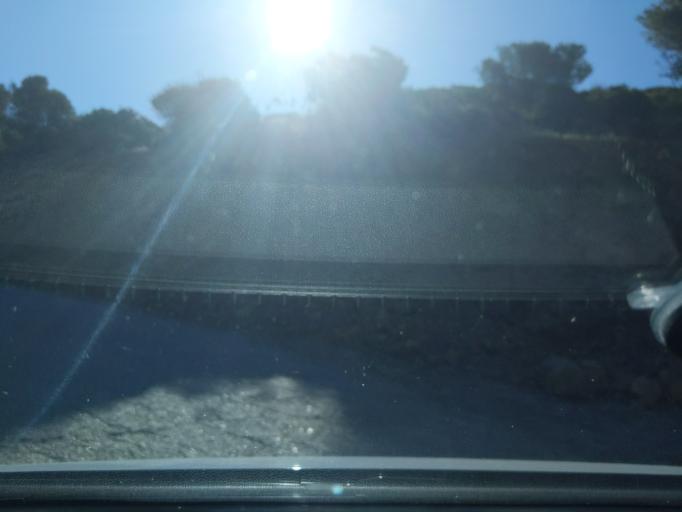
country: GR
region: Crete
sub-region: Nomos Irakleiou
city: Moires
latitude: 34.9381
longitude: 24.8140
